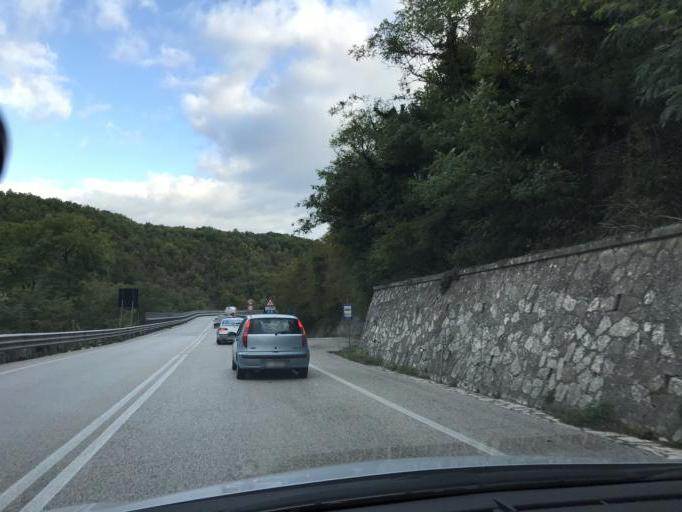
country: IT
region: Umbria
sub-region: Provincia di Terni
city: Ferentillo
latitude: 42.6746
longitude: 12.7265
